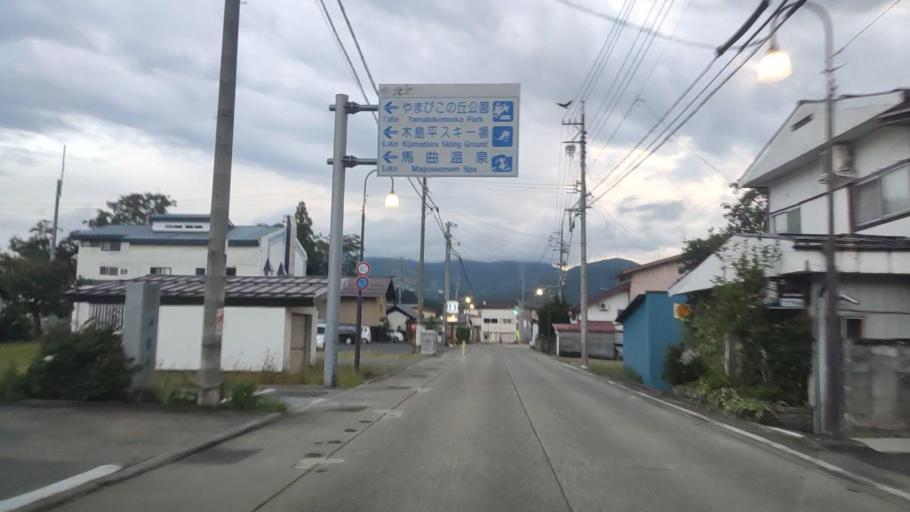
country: JP
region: Nagano
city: Iiyama
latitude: 36.8623
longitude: 138.4057
